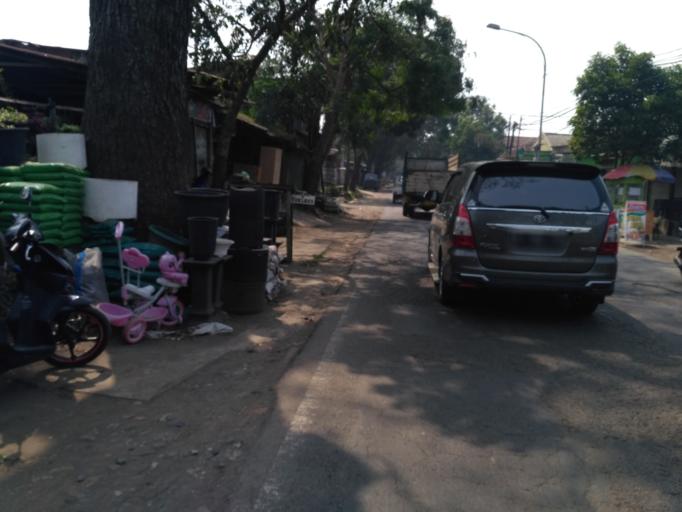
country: ID
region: East Java
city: Malang
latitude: -7.9865
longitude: 112.6546
